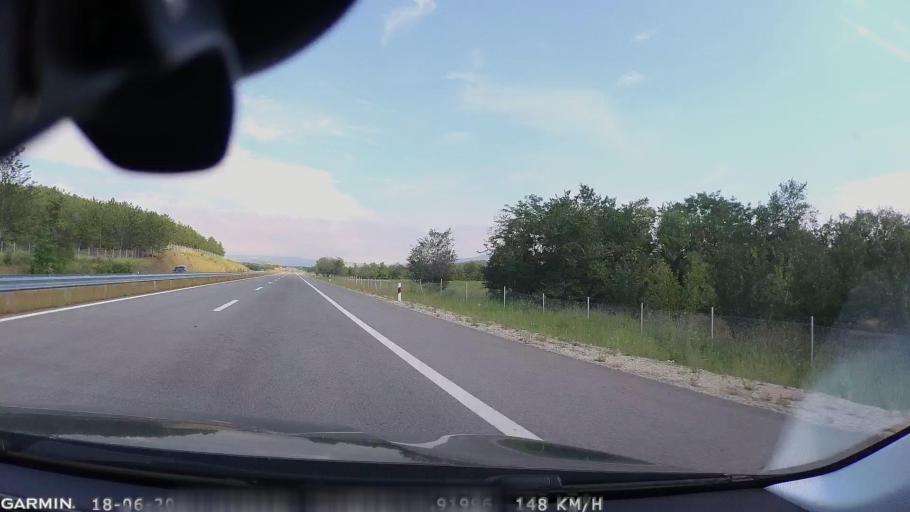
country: MK
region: Sveti Nikole
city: Sveti Nikole
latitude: 41.8988
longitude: 21.9180
